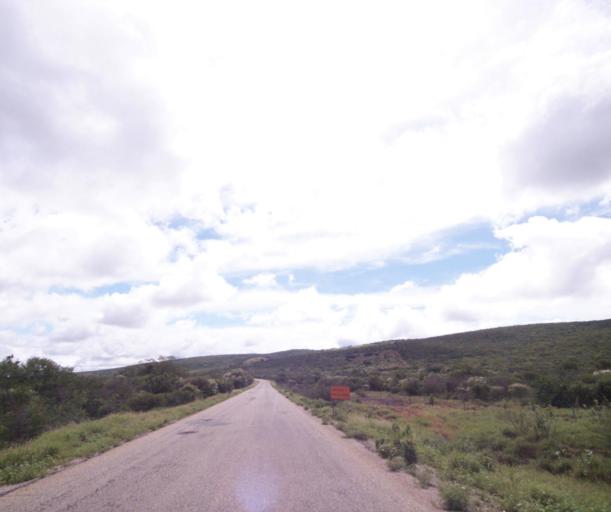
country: BR
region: Bahia
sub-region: Brumado
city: Brumado
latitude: -14.1975
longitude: -41.5882
